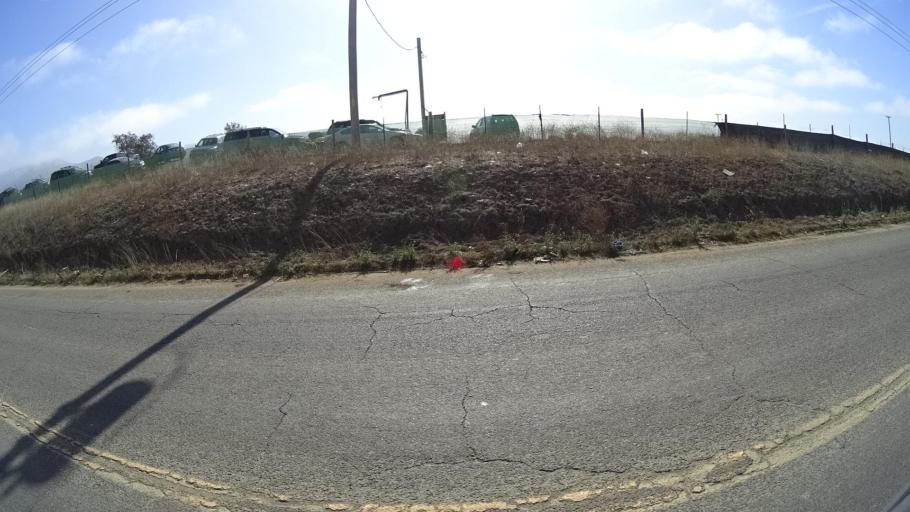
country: US
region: California
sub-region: Monterey County
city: Salinas
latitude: 36.7302
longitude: -121.6145
